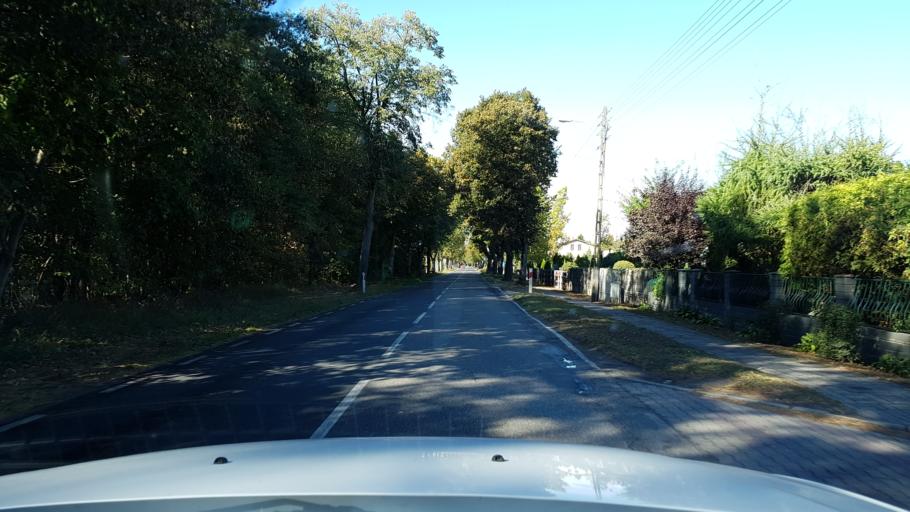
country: PL
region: West Pomeranian Voivodeship
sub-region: Powiat gryfinski
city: Gryfino
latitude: 53.2144
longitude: 14.4969
